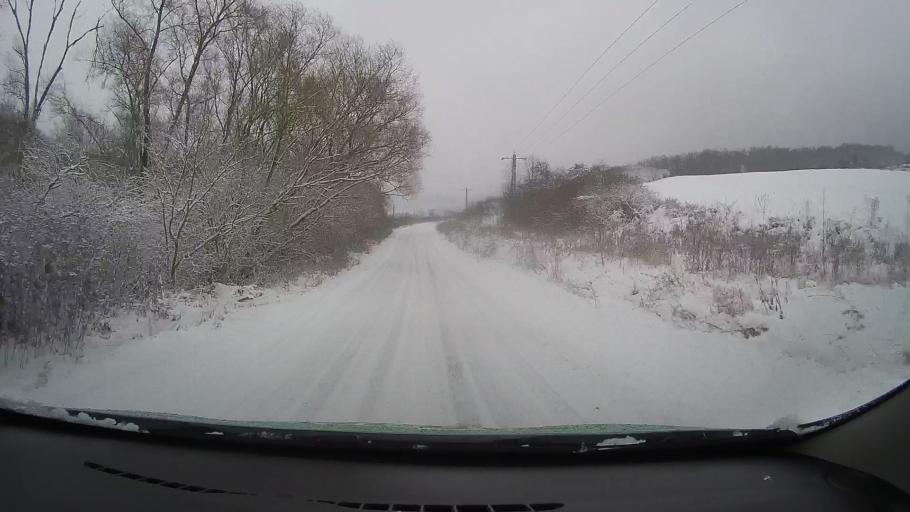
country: RO
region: Hunedoara
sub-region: Comuna Carjiti
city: Carjiti
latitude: 45.8396
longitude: 22.8357
